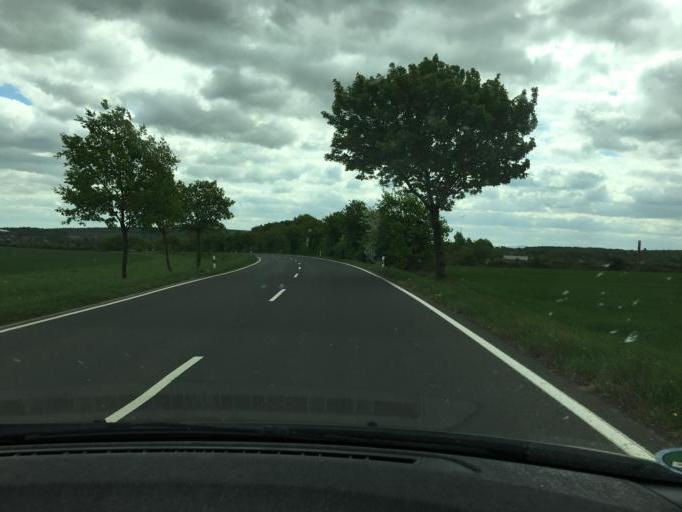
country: DE
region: North Rhine-Westphalia
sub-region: Regierungsbezirk Koln
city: Mechernich
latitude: 50.6365
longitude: 6.6778
